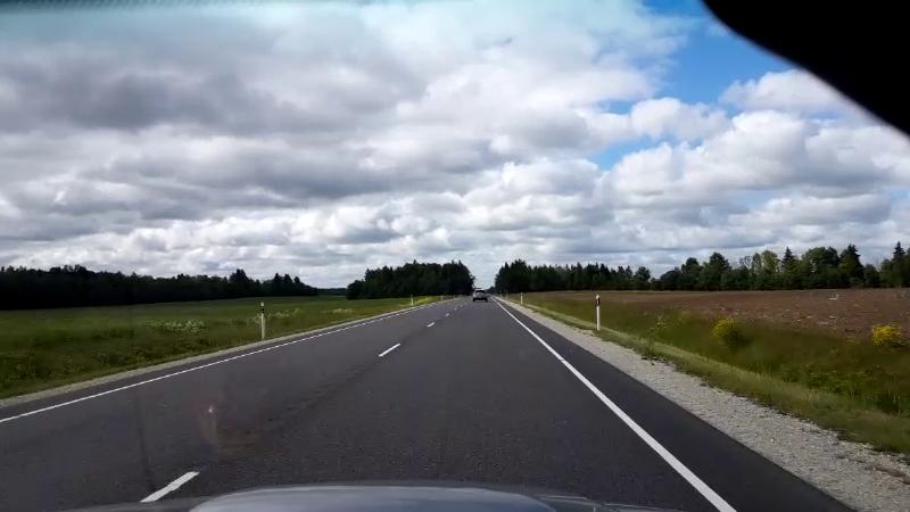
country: EE
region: Raplamaa
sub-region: Maerjamaa vald
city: Marjamaa
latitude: 58.8578
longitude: 24.4345
